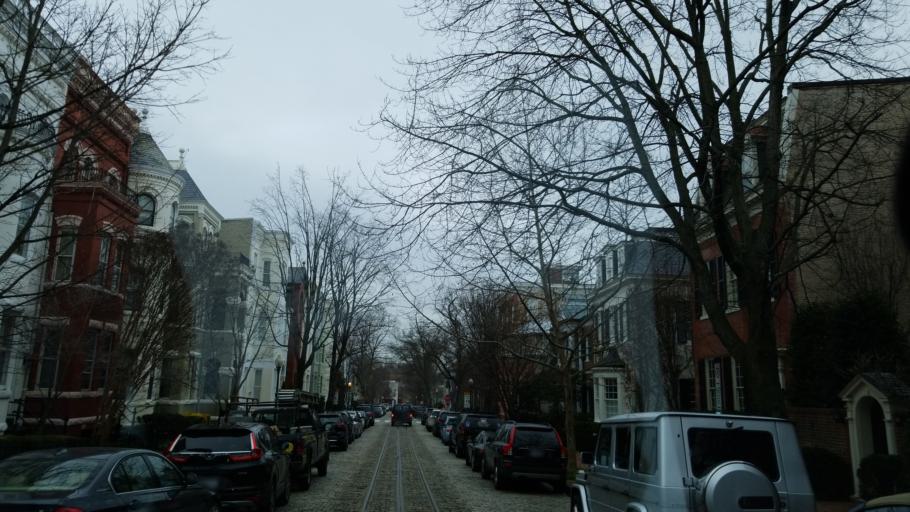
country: US
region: Washington, D.C.
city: Washington, D.C.
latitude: 38.9078
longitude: -77.0671
